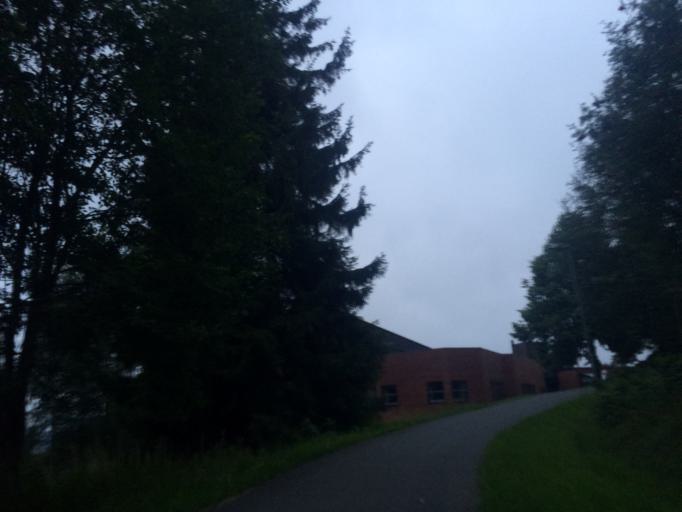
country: NO
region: Akershus
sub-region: Ski
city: Ski
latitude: 59.7200
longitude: 10.8315
